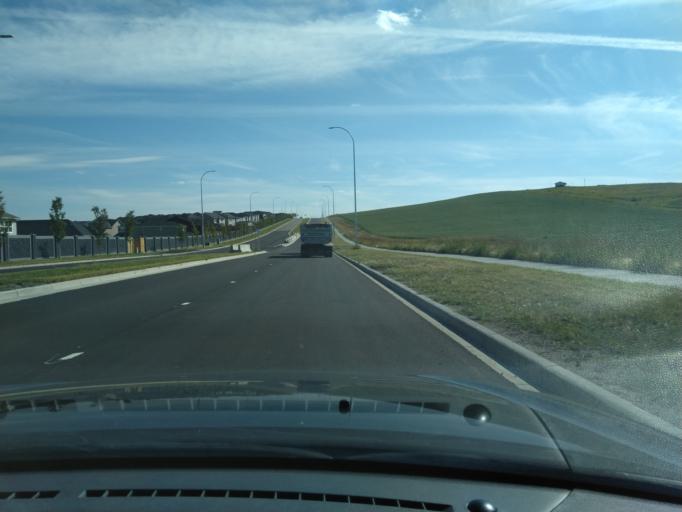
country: CA
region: Alberta
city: Calgary
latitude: 51.1813
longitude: -114.1762
